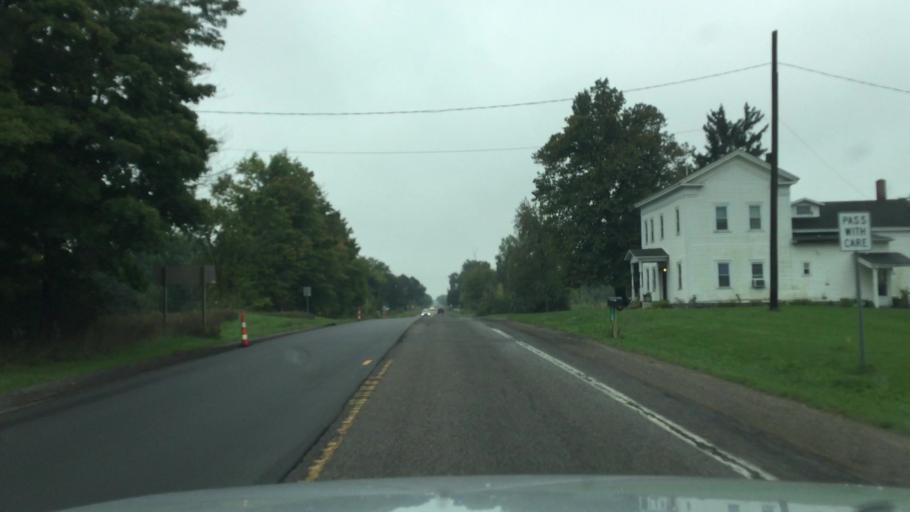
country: US
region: Michigan
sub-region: Shiawassee County
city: Owosso
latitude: 42.9338
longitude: -84.2226
